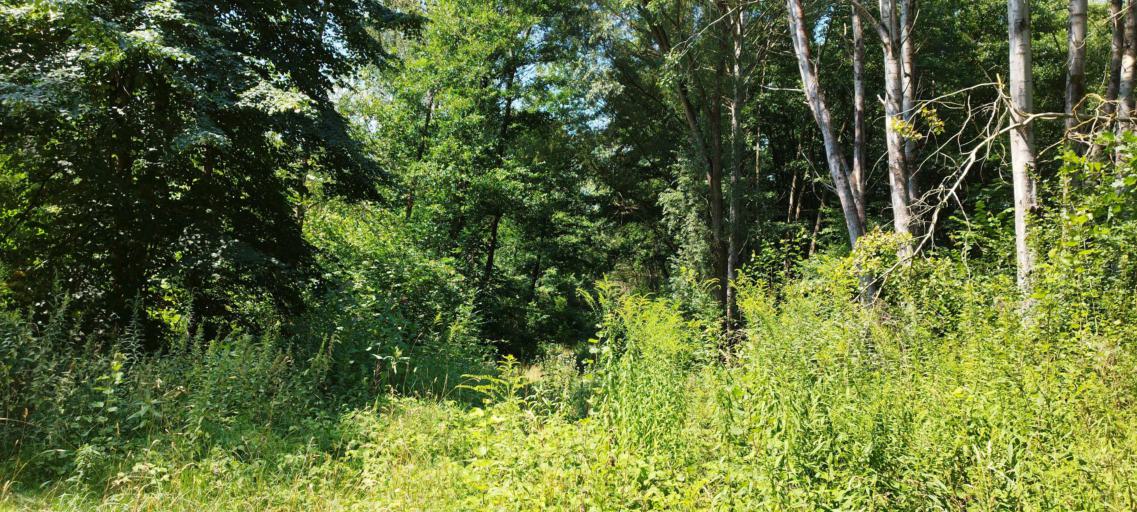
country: DE
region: Brandenburg
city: Petershagen
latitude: 52.5153
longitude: 13.8410
